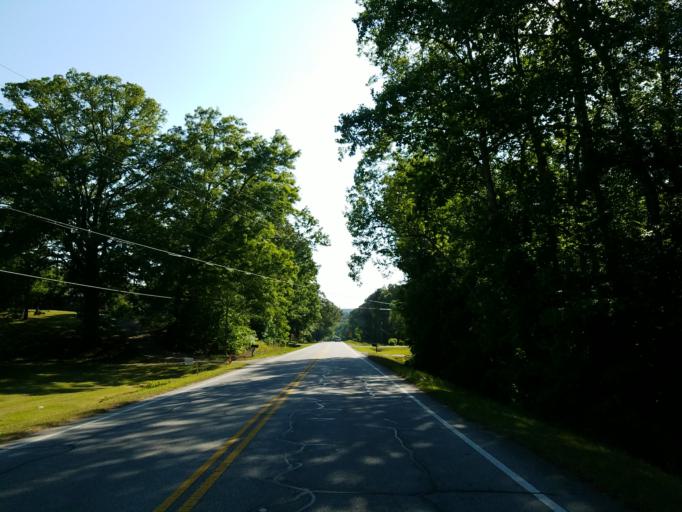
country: US
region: Georgia
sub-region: Paulding County
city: Dallas
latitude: 33.9103
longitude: -84.8654
